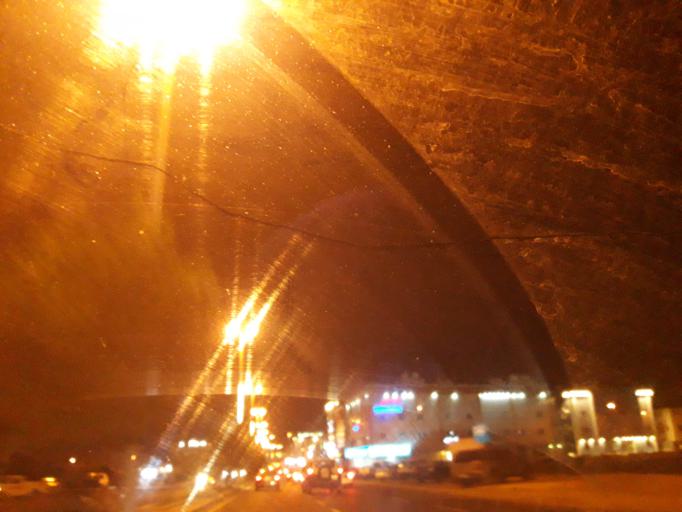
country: SA
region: Makkah
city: Ta'if
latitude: 21.3195
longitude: 40.4271
